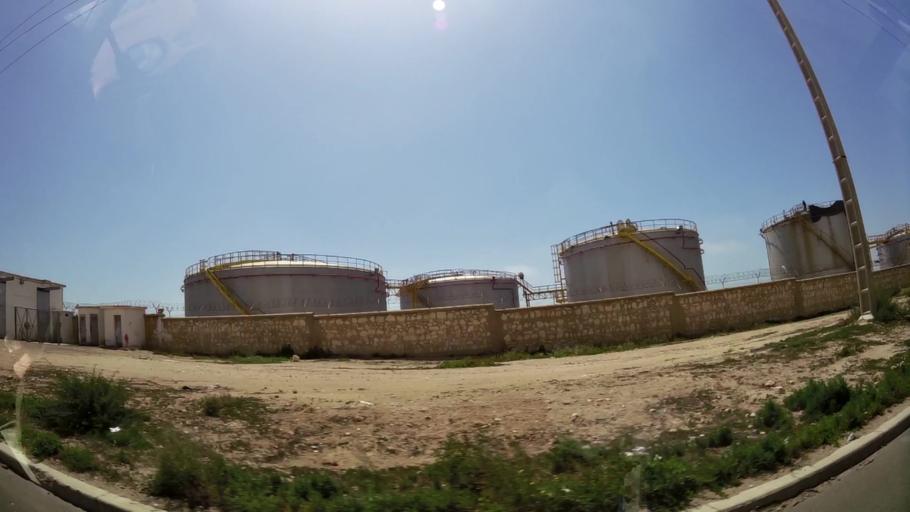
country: MA
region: Souss-Massa-Draa
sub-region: Agadir-Ida-ou-Tnan
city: Agadir
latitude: 30.4375
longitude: -9.6439
